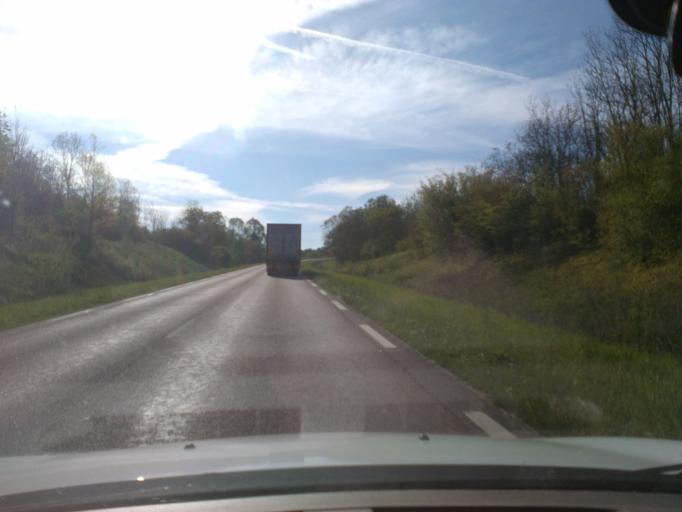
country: FR
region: Lorraine
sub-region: Departement des Vosges
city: Mirecourt
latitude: 48.3059
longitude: 6.1466
